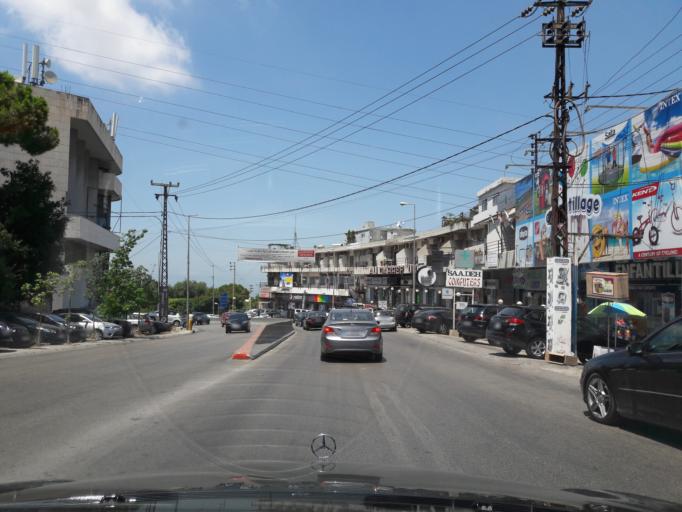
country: LB
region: Mont-Liban
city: Djounie
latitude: 33.9274
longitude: 35.6273
